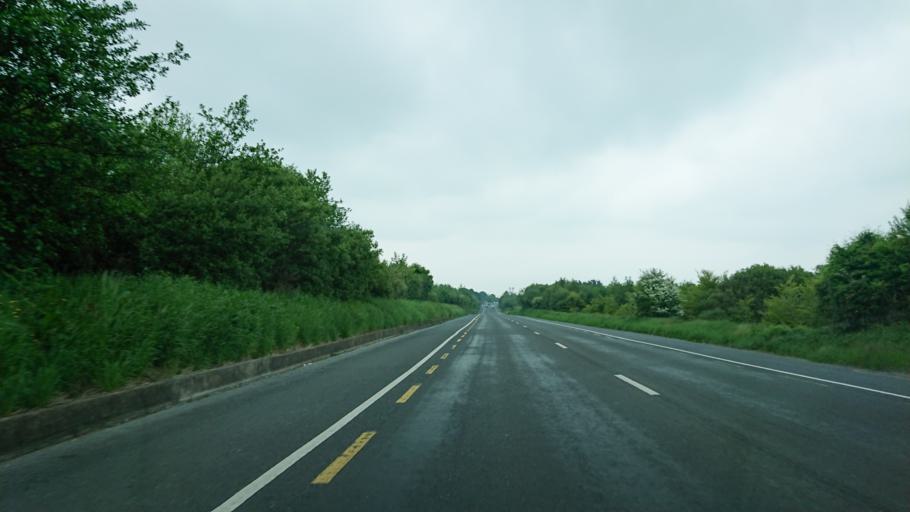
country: IE
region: Munster
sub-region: Waterford
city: Tra Mhor
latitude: 52.1871
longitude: -7.1287
